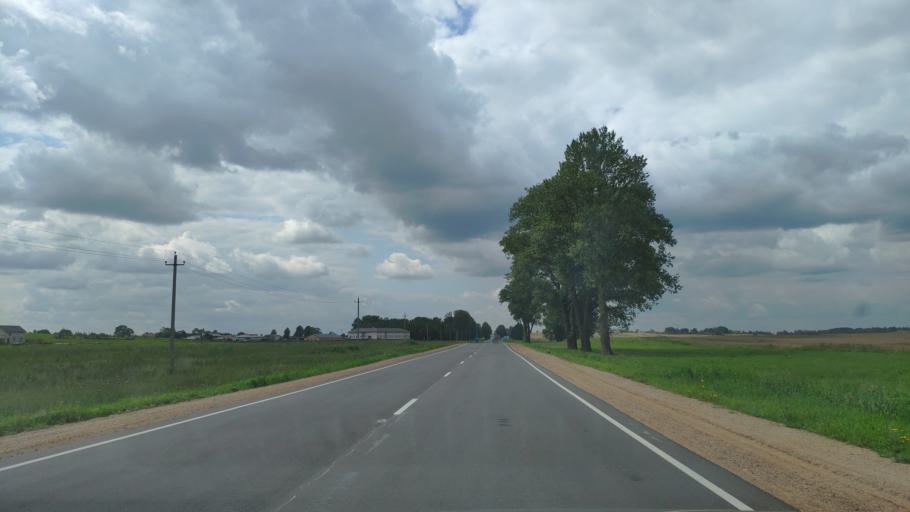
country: BY
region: Minsk
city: Zaslawye
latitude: 54.0057
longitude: 27.3418
